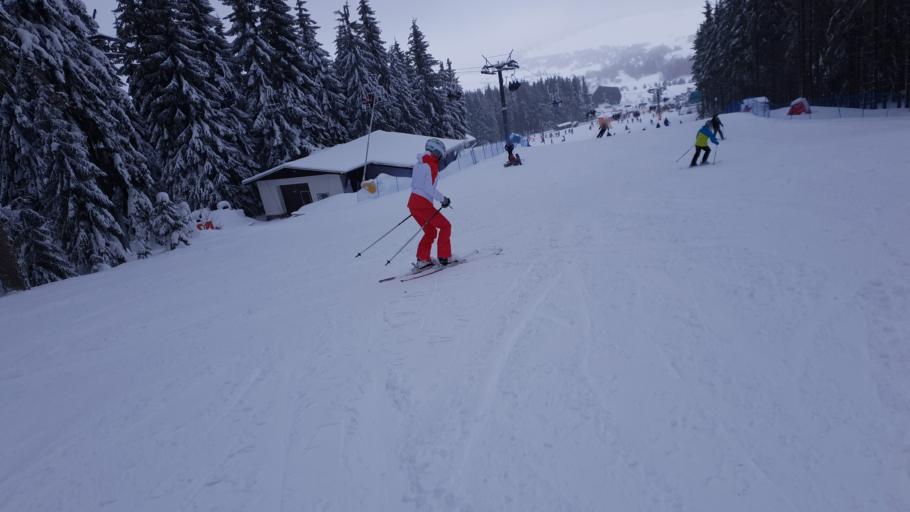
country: DE
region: Saxony
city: Kurort Oberwiesenthal
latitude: 50.4013
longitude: 12.9806
